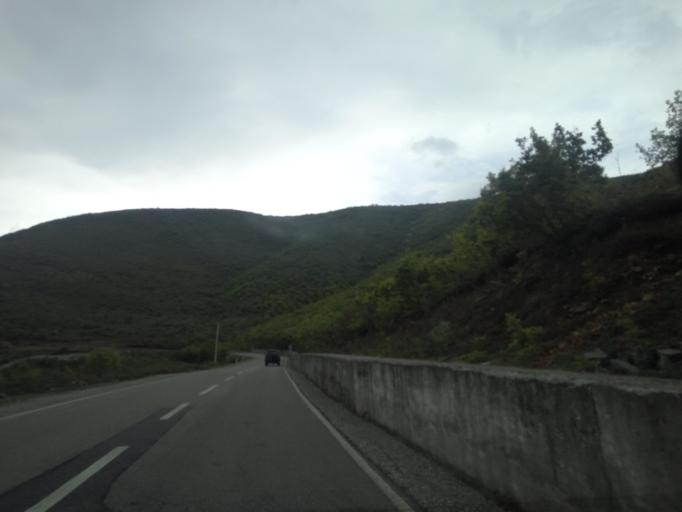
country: AL
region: Kukes
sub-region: Rrethi i Tropojes
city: Bytyc
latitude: 42.4002
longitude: 20.1976
